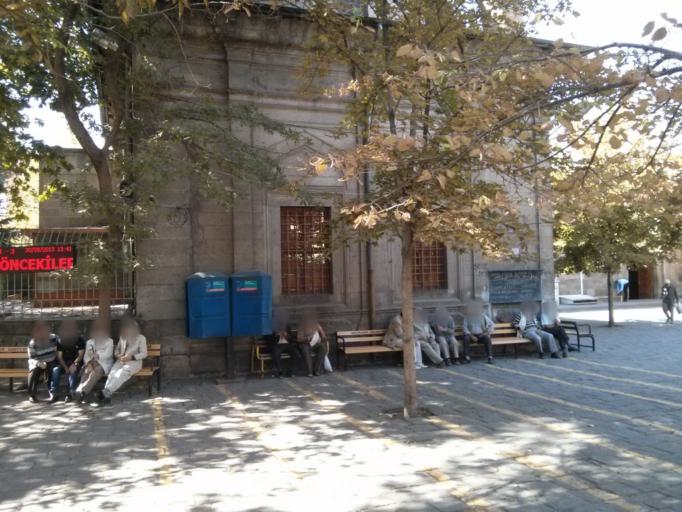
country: TR
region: Kayseri
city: Kayseri
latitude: 38.7198
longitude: 35.4867
